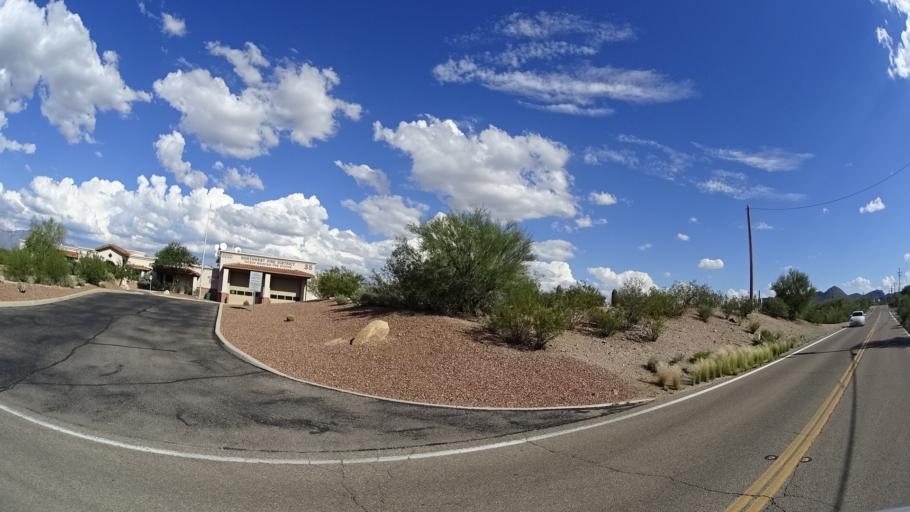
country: US
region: Arizona
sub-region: Pima County
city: Flowing Wells
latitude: 32.2657
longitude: -111.0628
